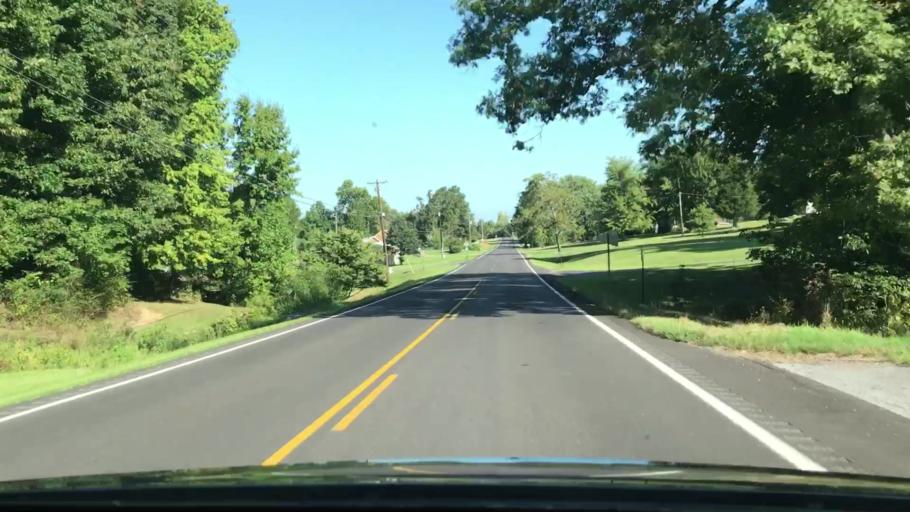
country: US
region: Kentucky
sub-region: Marshall County
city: Benton
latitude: 36.7714
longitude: -88.4403
